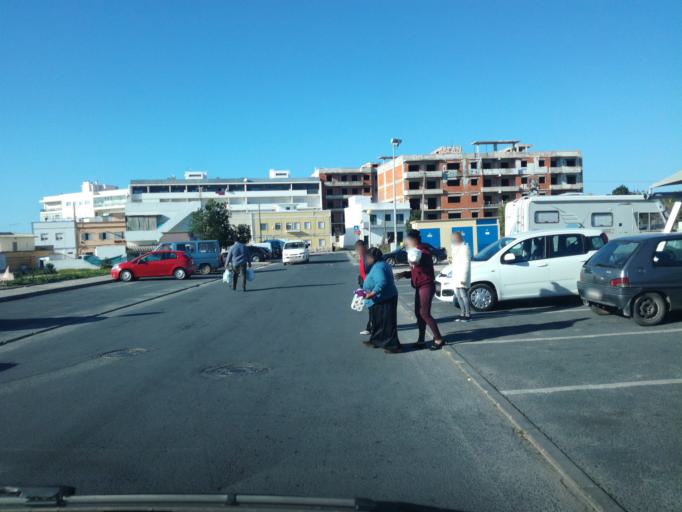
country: PT
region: Faro
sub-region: Olhao
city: Olhao
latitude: 37.0369
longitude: -7.8324
